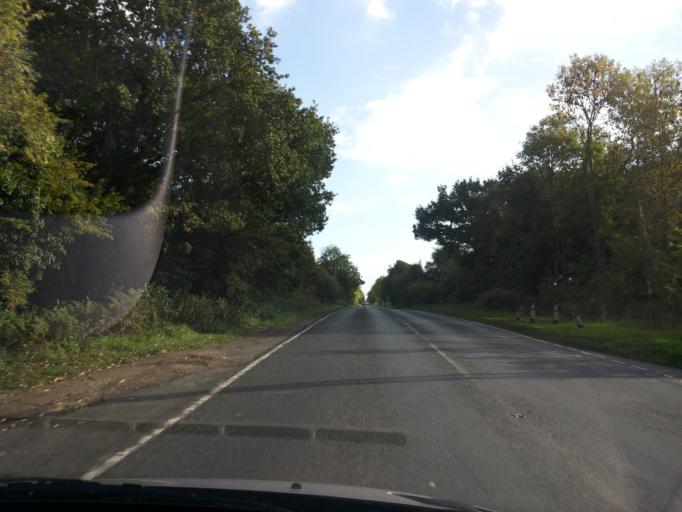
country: GB
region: England
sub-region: North Yorkshire
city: Camblesforth
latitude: 53.7465
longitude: -1.0499
